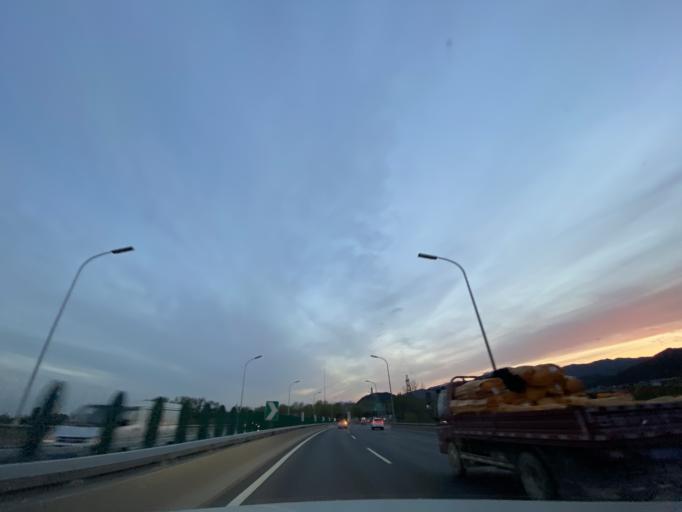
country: CN
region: Beijing
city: Haidian
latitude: 40.0039
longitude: 116.2629
